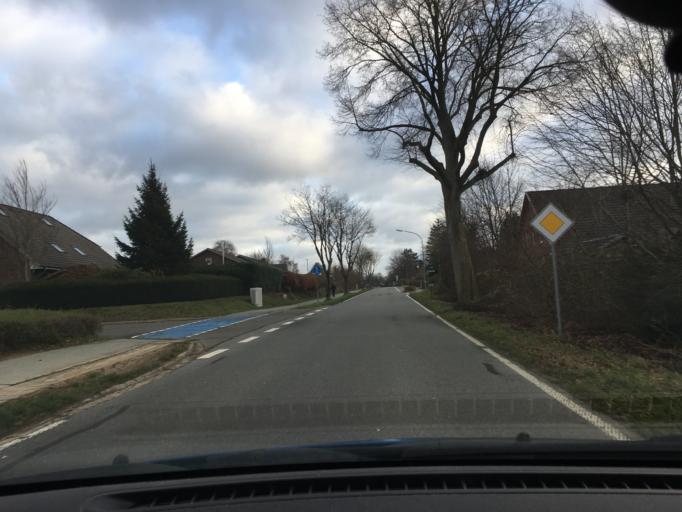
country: DE
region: Schleswig-Holstein
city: Schenefeld
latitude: 54.0483
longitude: 9.4728
